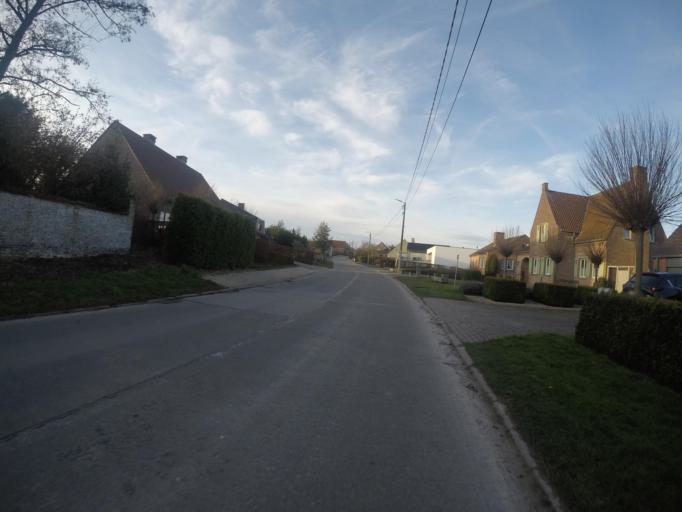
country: BE
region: Flanders
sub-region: Provincie Vlaams-Brabant
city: Pepingen
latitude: 50.7412
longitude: 4.1818
